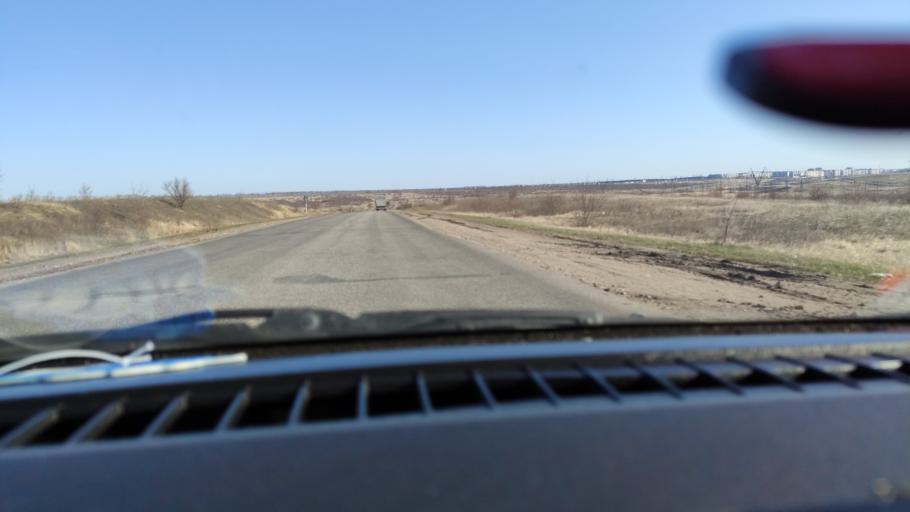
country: RU
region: Samara
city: Varlamovo
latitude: 53.0861
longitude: 48.3548
